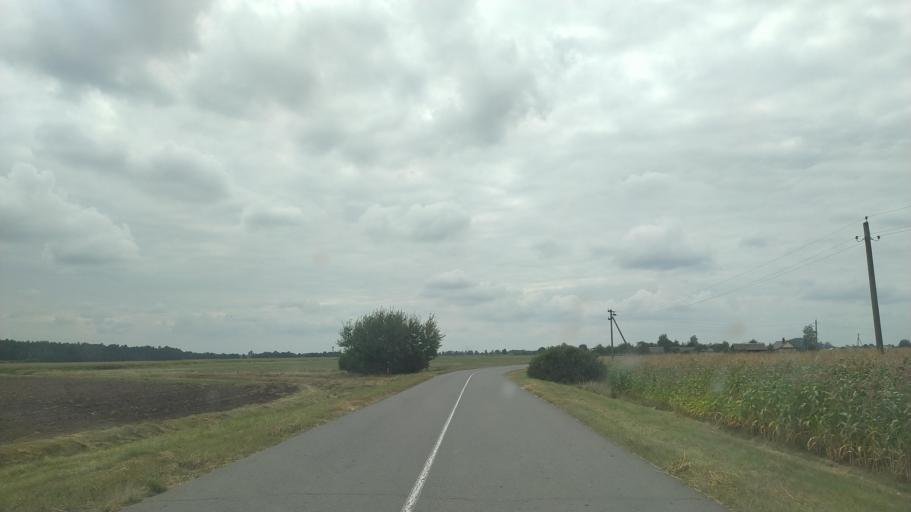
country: BY
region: Brest
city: Byelaazyorsk
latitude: 52.5397
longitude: 25.1242
